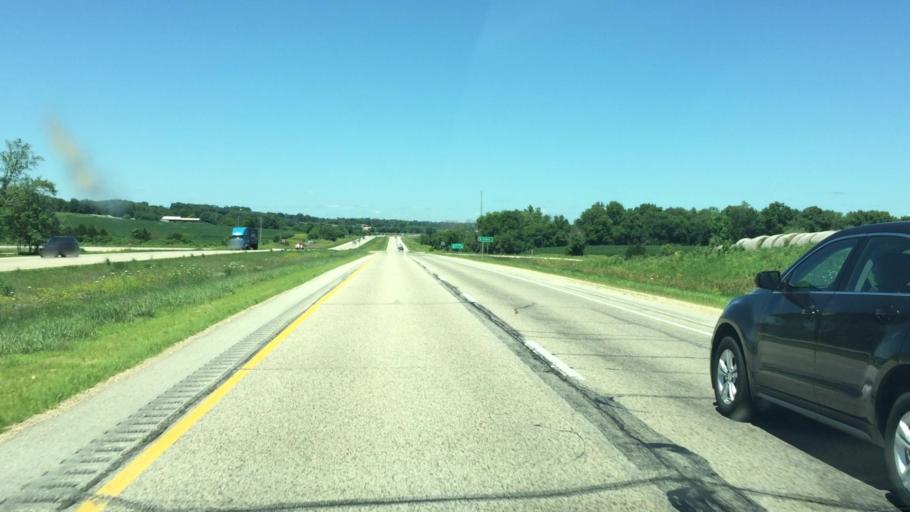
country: US
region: Iowa
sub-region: Jackson County
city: Maquoketa
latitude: 42.1535
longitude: -90.6761
